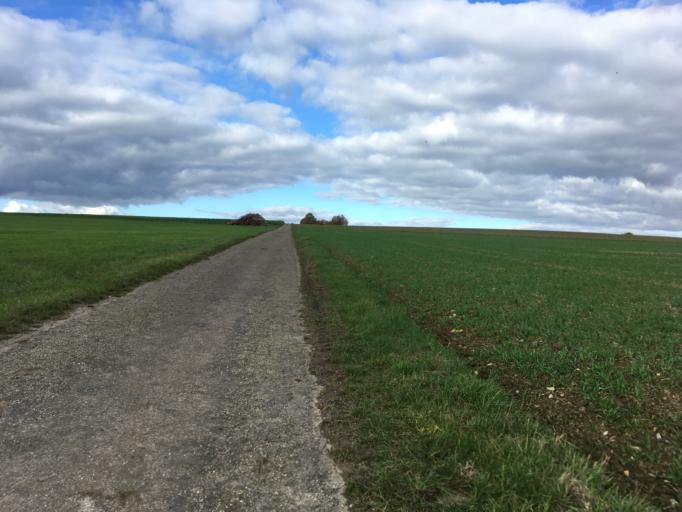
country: DE
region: Baden-Wuerttemberg
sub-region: Regierungsbezirk Stuttgart
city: Untermunkheim
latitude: 49.1950
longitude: 9.7404
